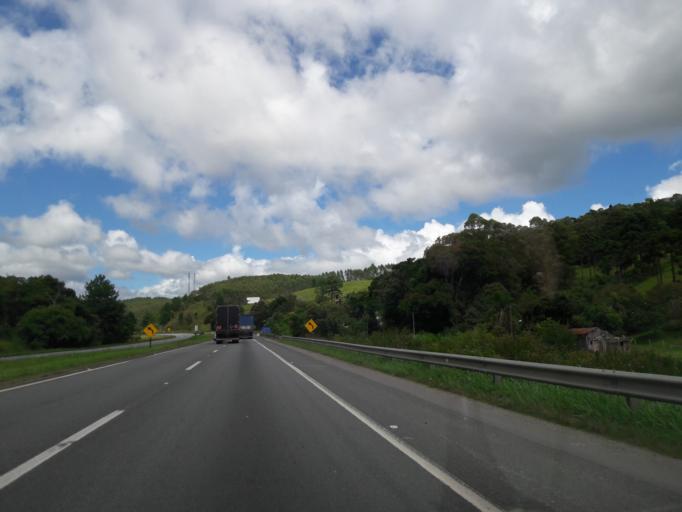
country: BR
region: Parana
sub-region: Campina Grande Do Sul
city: Campina Grande do Sul
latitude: -25.1247
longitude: -48.8567
